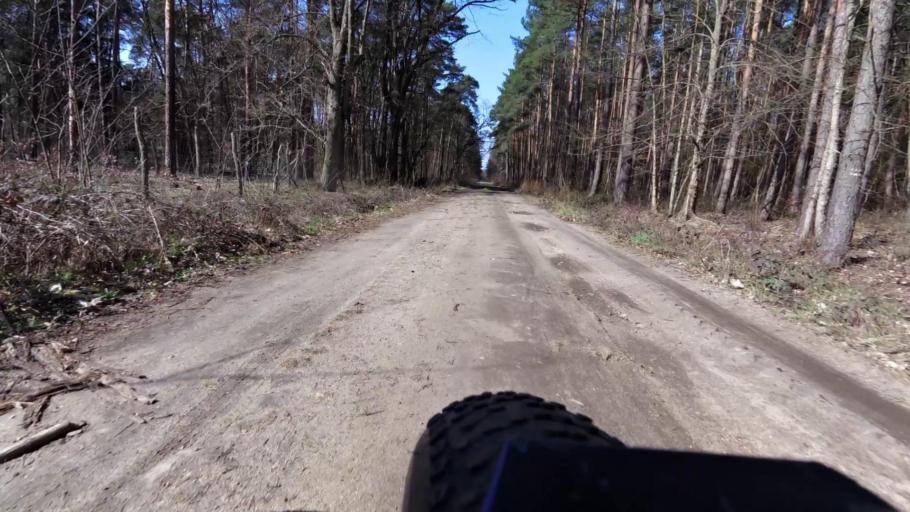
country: PL
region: Lubusz
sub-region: Powiat slubicki
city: Cybinka
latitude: 52.2118
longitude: 14.8603
